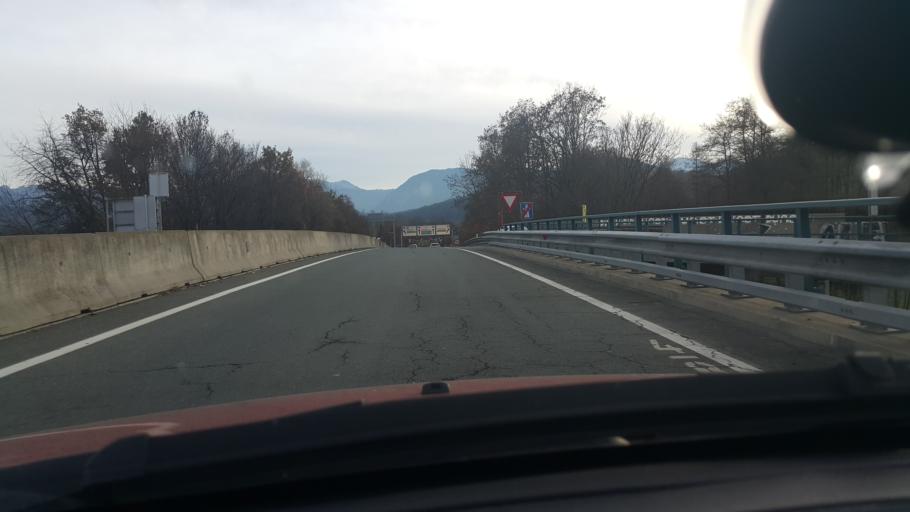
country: AT
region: Carinthia
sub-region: Klagenfurt am Woerthersee
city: Klagenfurt am Woerthersee
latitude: 46.6235
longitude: 14.2627
